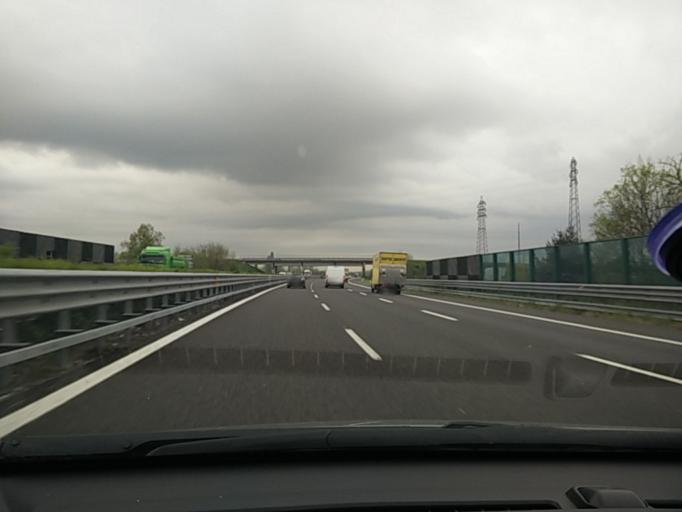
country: IT
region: Veneto
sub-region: Provincia di Treviso
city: Carbonera
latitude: 45.7167
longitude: 12.2904
